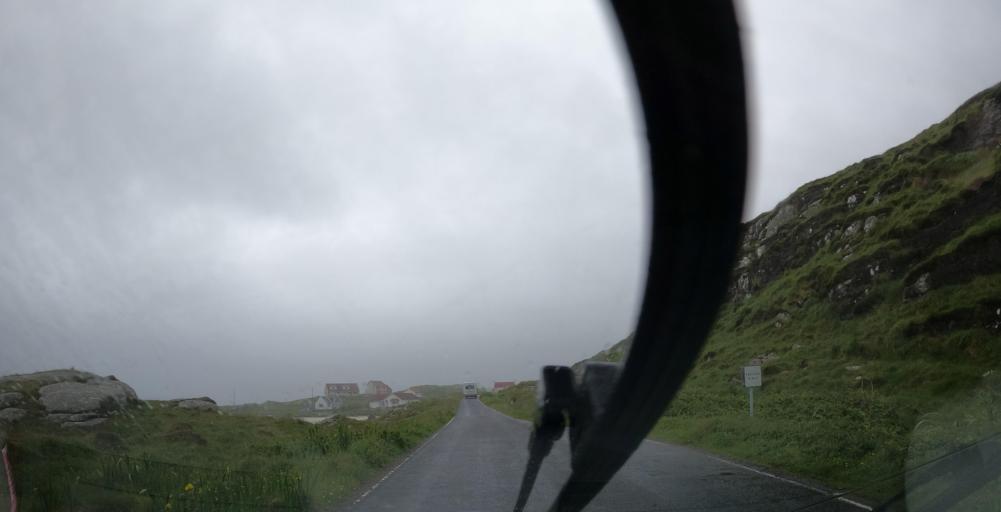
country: GB
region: Scotland
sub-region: Eilean Siar
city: Barra
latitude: 57.0155
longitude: -7.4337
